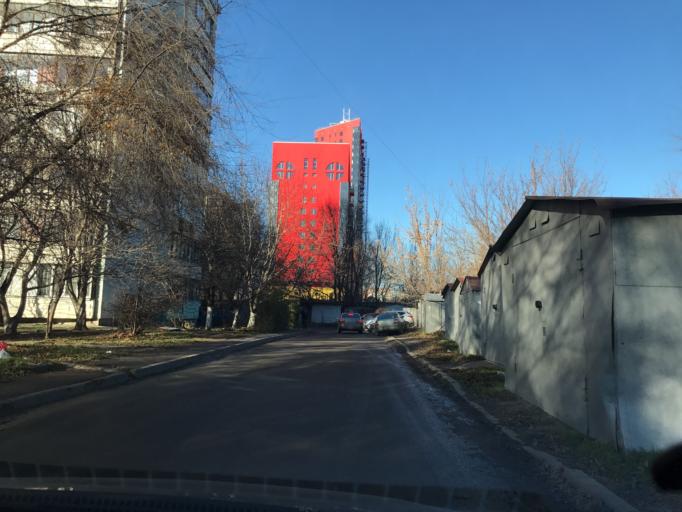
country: RU
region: Rostov
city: Rostov-na-Donu
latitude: 47.2142
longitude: 39.6228
